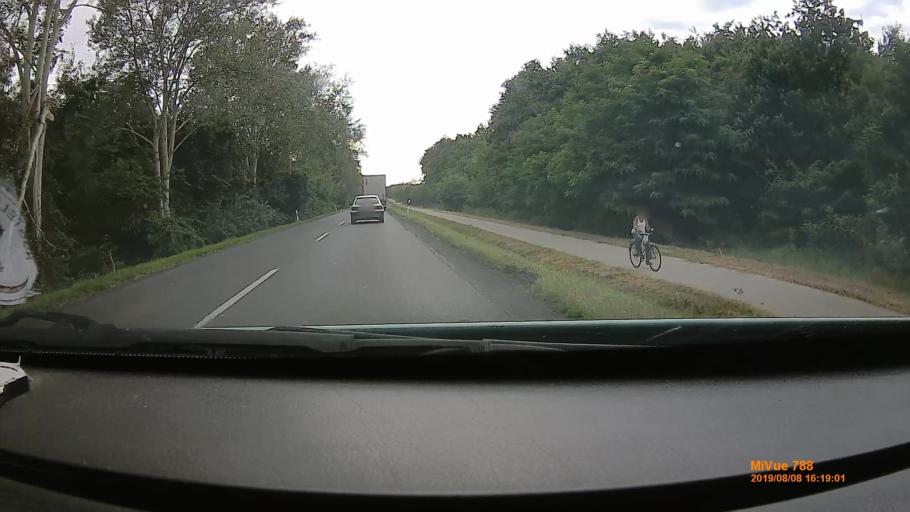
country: HU
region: Szabolcs-Szatmar-Bereg
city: Mateszalka
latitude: 47.9654
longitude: 22.2794
